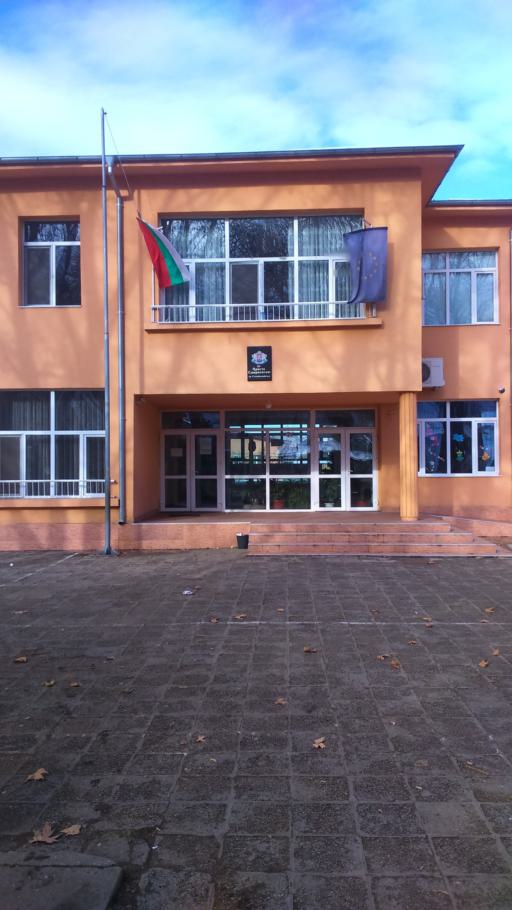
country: BG
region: Plovdiv
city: Stamboliyski
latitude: 42.1287
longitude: 24.5396
